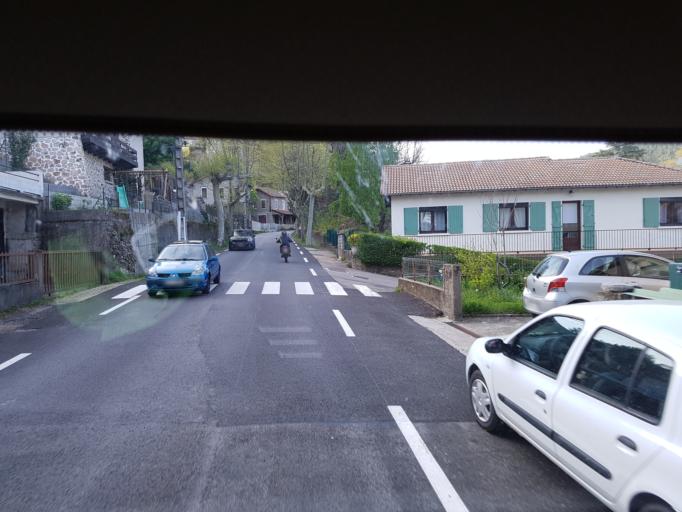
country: FR
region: Languedoc-Roussillon
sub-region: Departement du Gard
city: Branoux-les-Taillades
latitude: 44.3468
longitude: 3.9494
